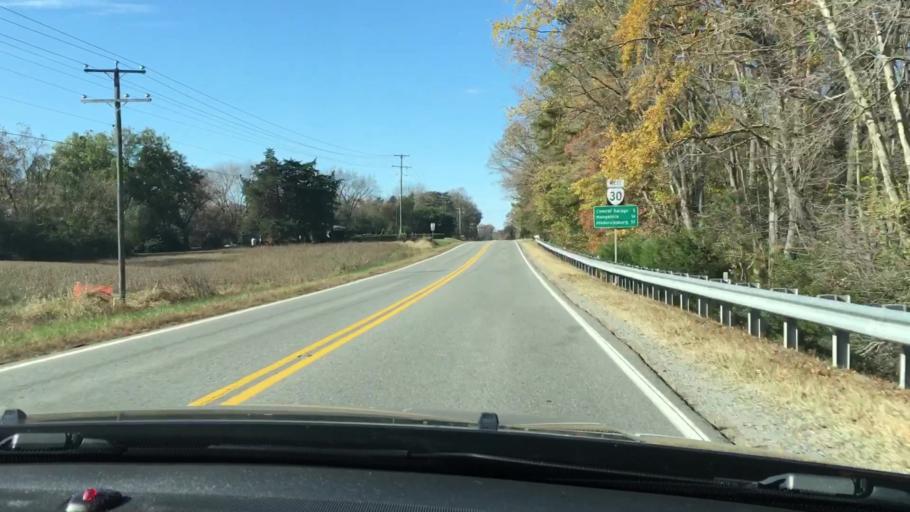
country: US
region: Virginia
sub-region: King William County
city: King William
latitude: 37.7044
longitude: -77.0482
